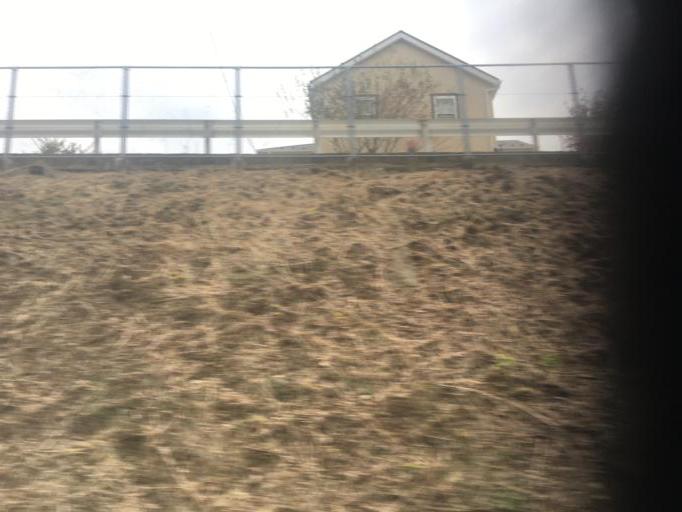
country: JP
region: Tokyo
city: Hachioji
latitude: 35.6626
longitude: 139.3593
